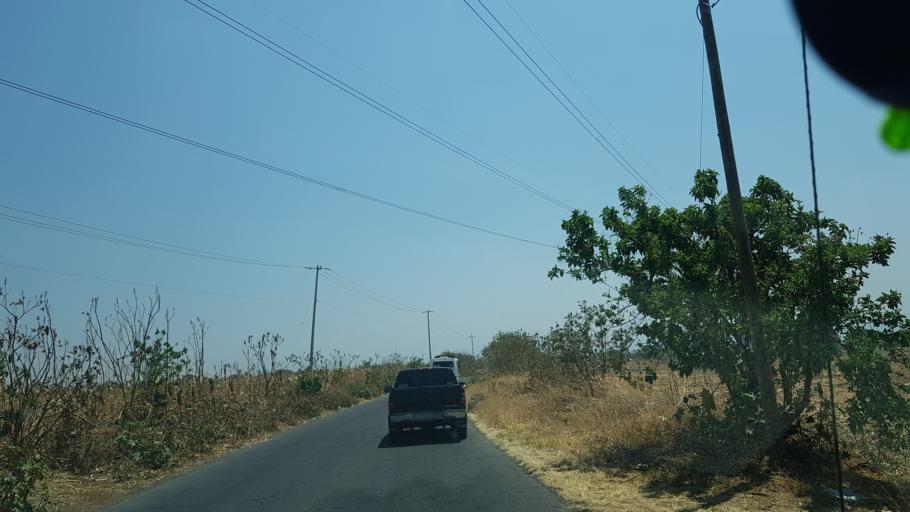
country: MX
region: Puebla
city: Tochimilco
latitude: 18.8896
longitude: -98.5254
